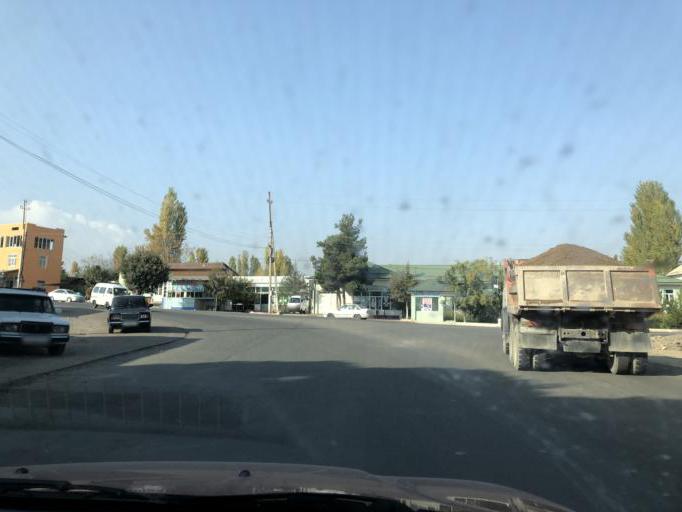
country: UZ
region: Namangan
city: Chust Shahri
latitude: 41.0730
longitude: 71.2044
